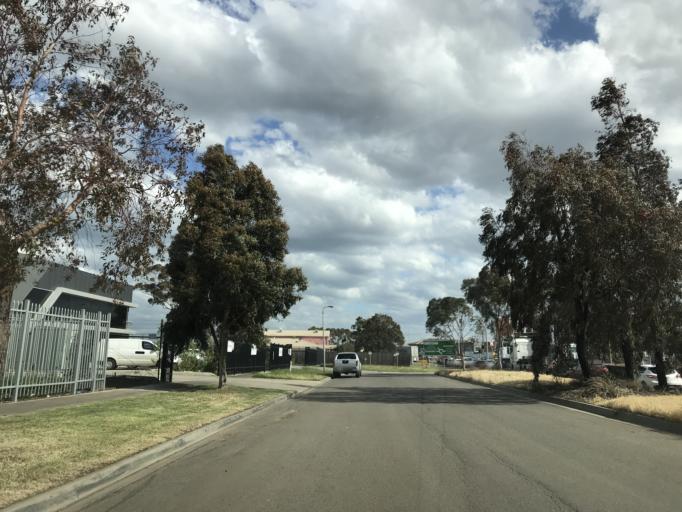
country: AU
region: Victoria
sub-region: Brimbank
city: Sunshine West
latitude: -37.8146
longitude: 144.8175
